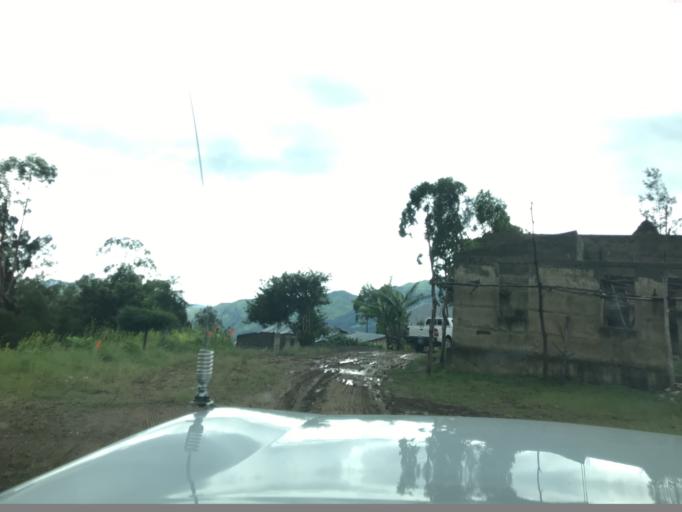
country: TL
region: Aileu
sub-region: Aileu Villa
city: Aileu
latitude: -8.8609
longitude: 125.5668
